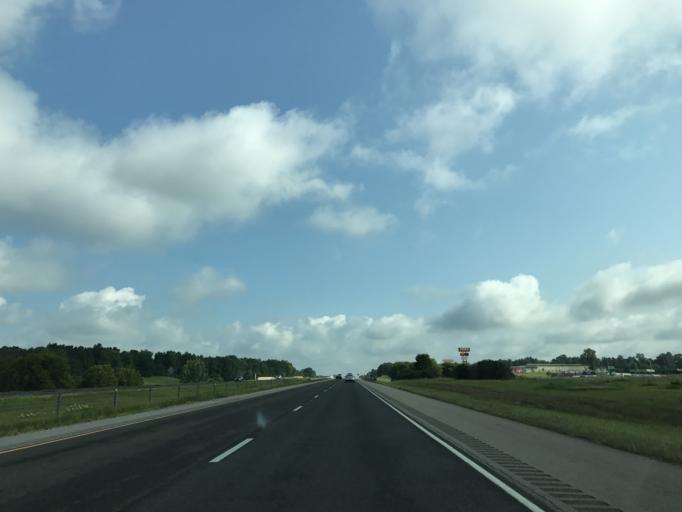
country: US
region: Indiana
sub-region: Steuben County
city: Fremont
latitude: 41.7450
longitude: -84.9971
